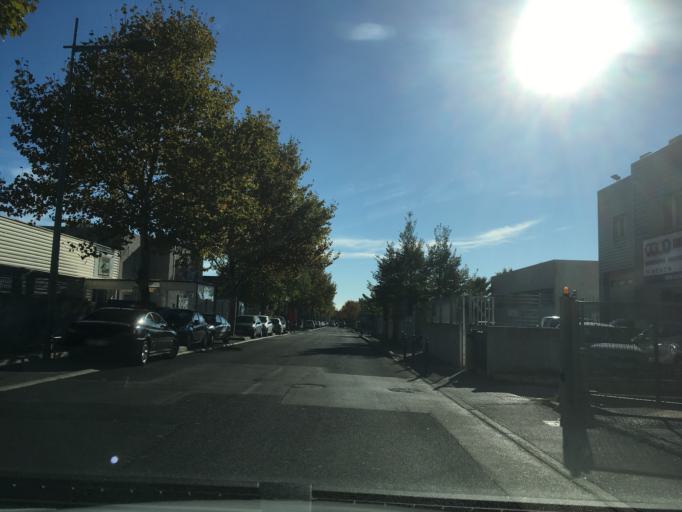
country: FR
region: Languedoc-Roussillon
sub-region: Departement de l'Herault
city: Juvignac
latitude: 43.6218
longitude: 3.8210
